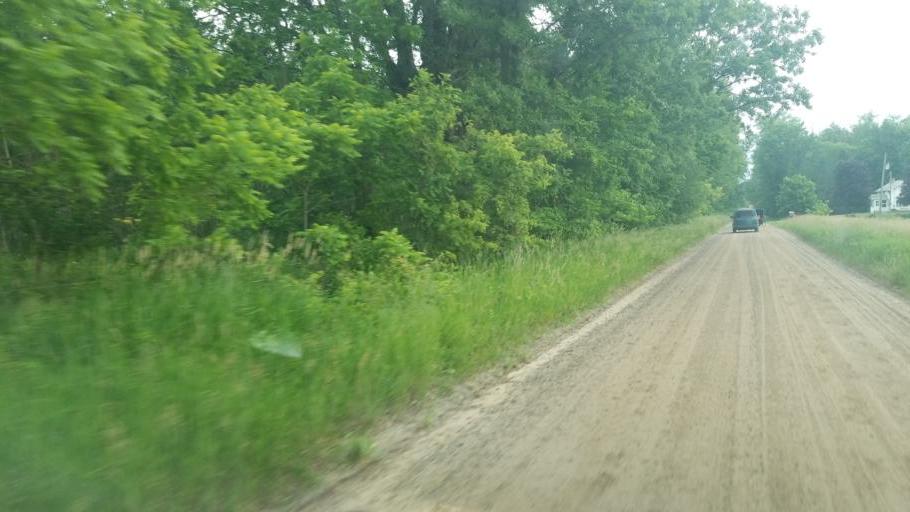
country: US
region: Michigan
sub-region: Barry County
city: Nashville
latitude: 42.6145
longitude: -84.9757
